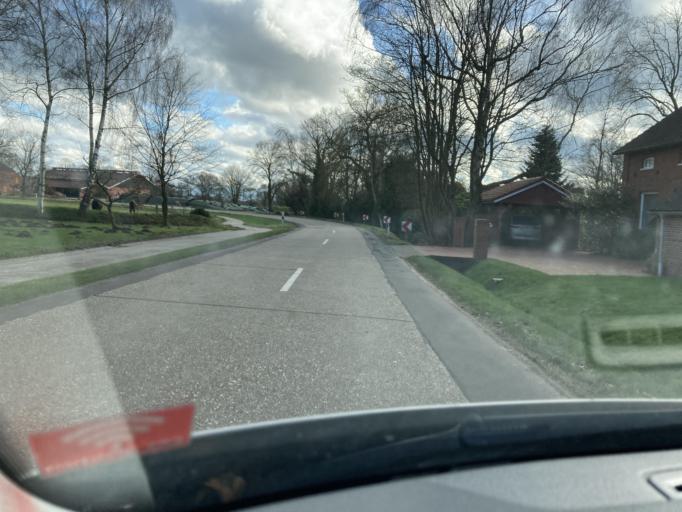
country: DE
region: Lower Saxony
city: Filsum
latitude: 53.2381
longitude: 7.6537
